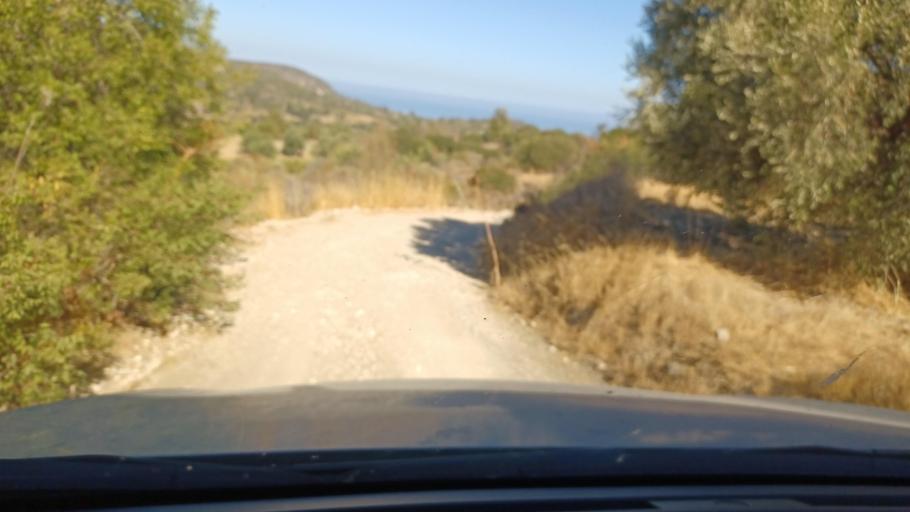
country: CY
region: Pafos
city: Polis
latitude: 34.9996
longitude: 32.5056
